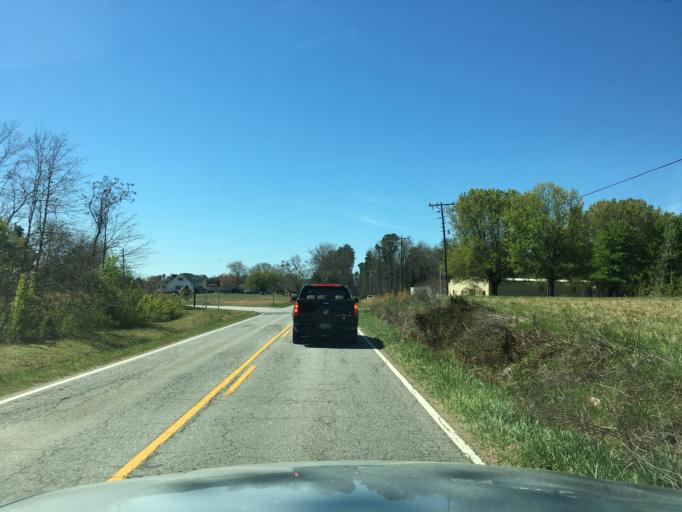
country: US
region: South Carolina
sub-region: Spartanburg County
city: Roebuck
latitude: 34.8818
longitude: -81.9848
